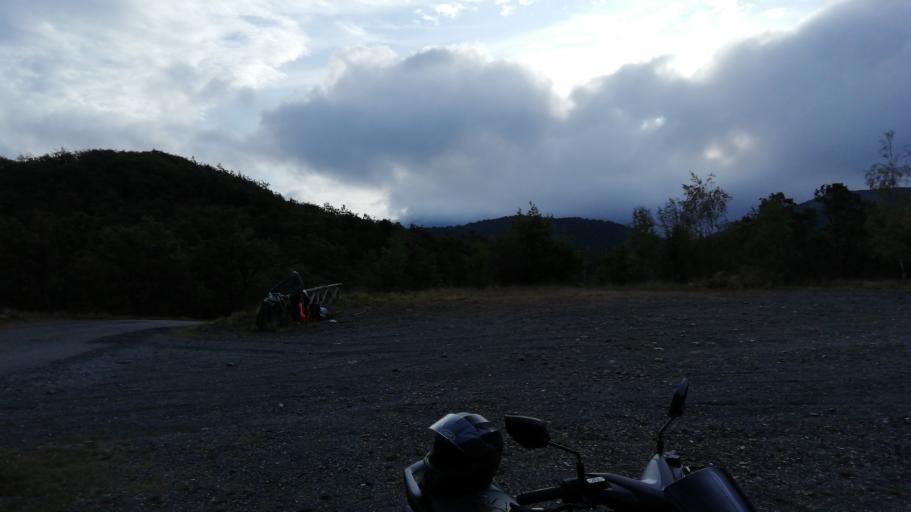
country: IT
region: Piedmont
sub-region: Provincia di Alessandria
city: Voltaggio
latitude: 44.5665
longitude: 8.7884
